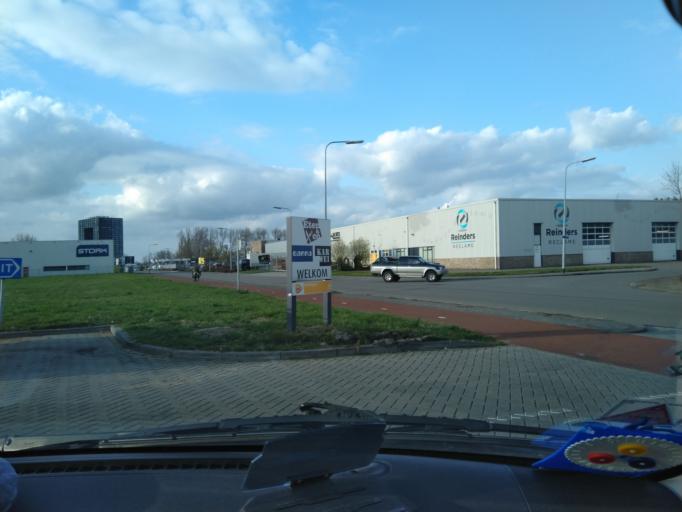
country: NL
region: Groningen
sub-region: Gemeente Groningen
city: Oosterpark
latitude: 53.2178
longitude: 6.6041
